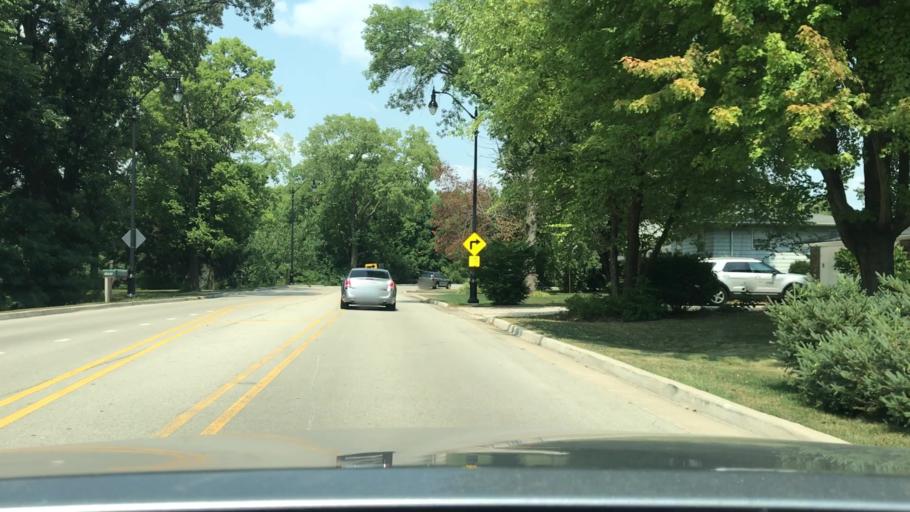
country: US
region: Illinois
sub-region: Will County
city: Plainfield
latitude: 41.5943
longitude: -88.2210
